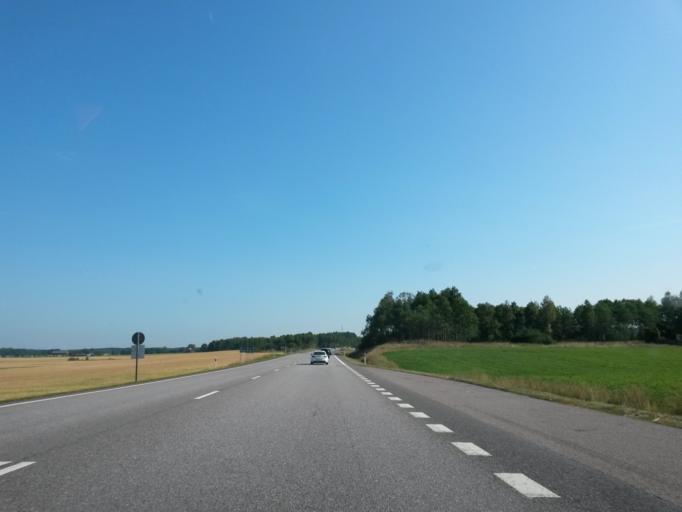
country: SE
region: Vaestra Goetaland
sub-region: Vargarda Kommun
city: Vargarda
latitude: 58.1126
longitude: 12.8424
